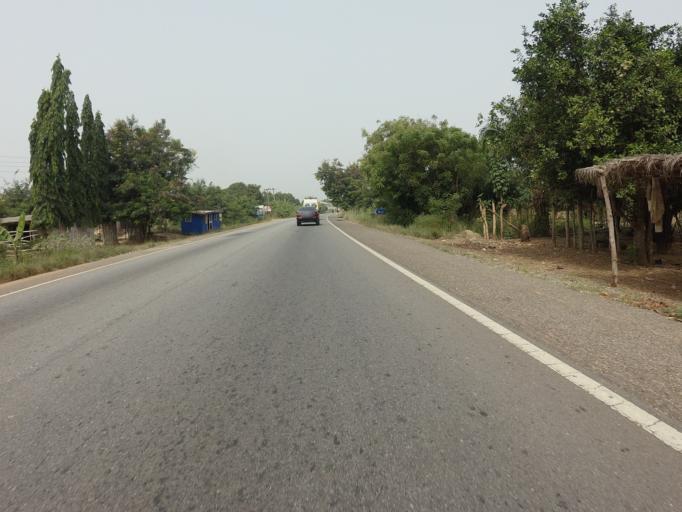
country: GH
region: Volta
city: Anloga
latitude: 5.9930
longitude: 0.5683
